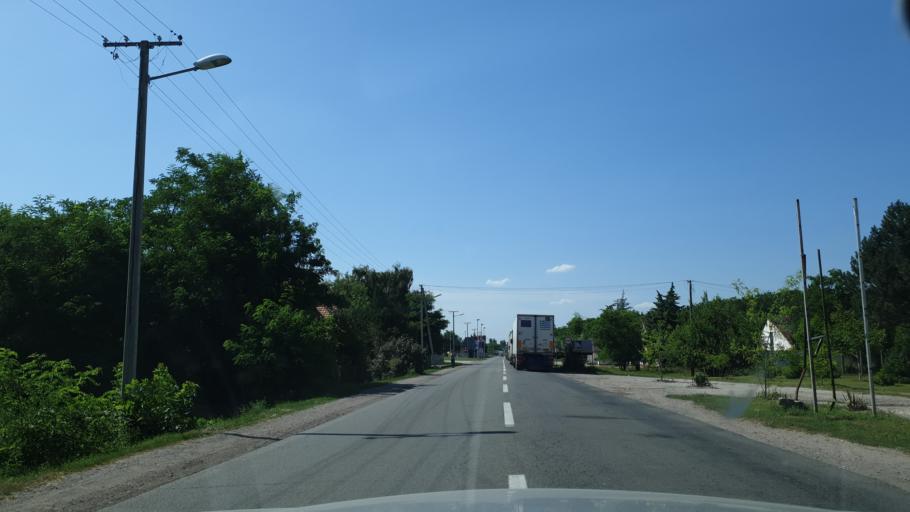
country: HU
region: Bacs-Kiskun
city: Tompa
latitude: 46.1580
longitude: 19.5705
